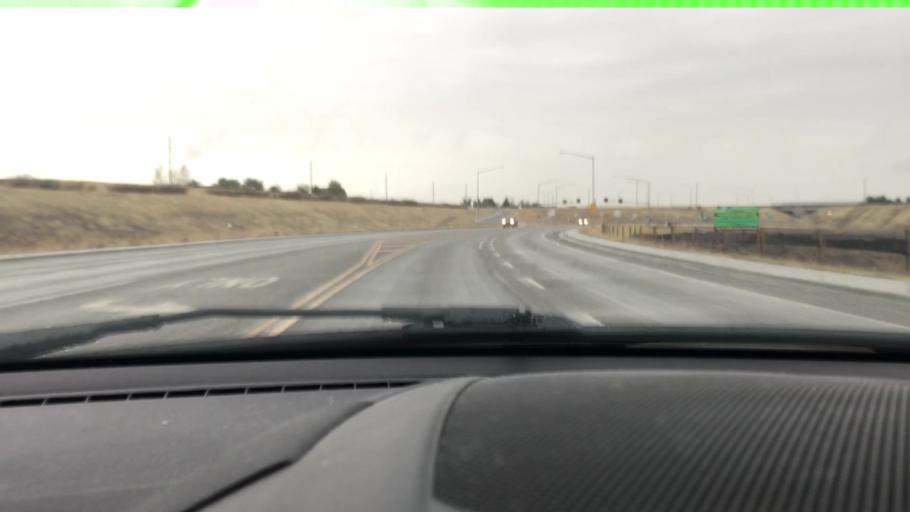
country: US
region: Montana
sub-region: Gallatin County
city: Belgrade
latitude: 45.7633
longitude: -111.1627
